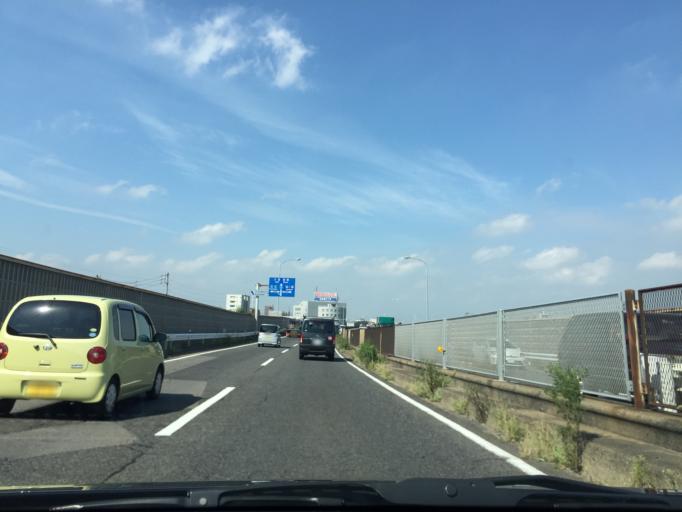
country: JP
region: Gifu
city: Kasamatsucho
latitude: 35.3880
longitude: 136.7683
